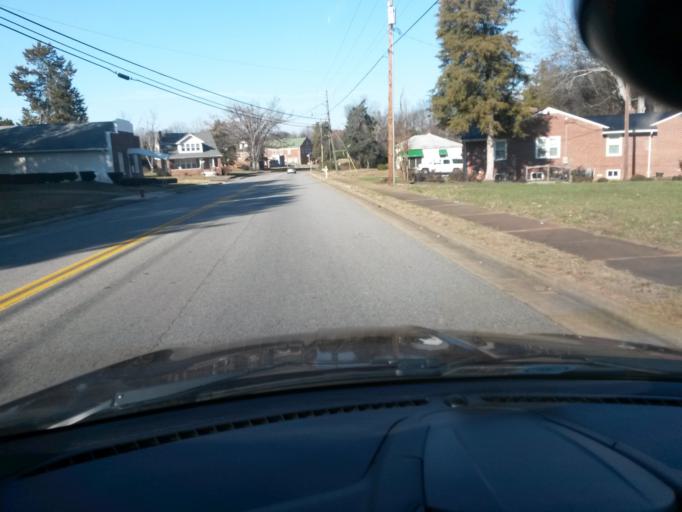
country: US
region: Virginia
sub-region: Charlotte County
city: Charlotte Court House
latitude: 37.0613
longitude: -78.6343
